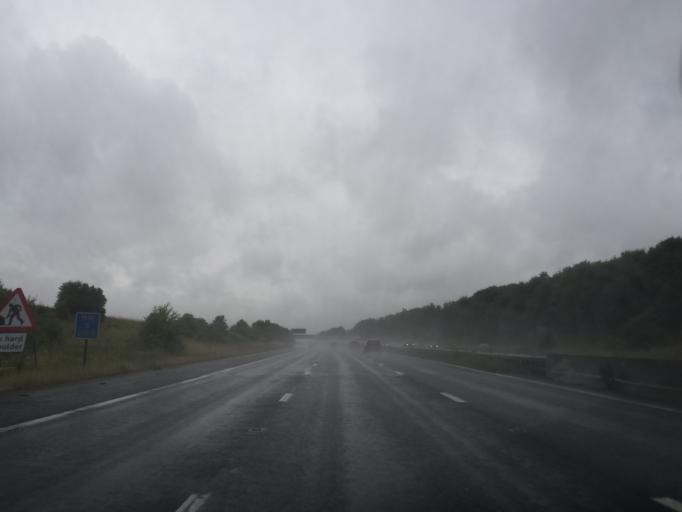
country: GB
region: England
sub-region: Rotherham
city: Hellaby
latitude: 53.4226
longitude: -1.2518
